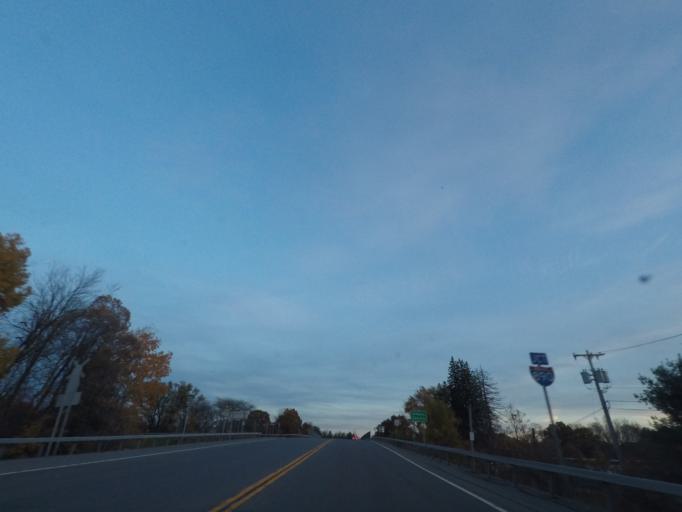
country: US
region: New York
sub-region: Schenectady County
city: Rotterdam
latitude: 42.7608
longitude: -73.9338
